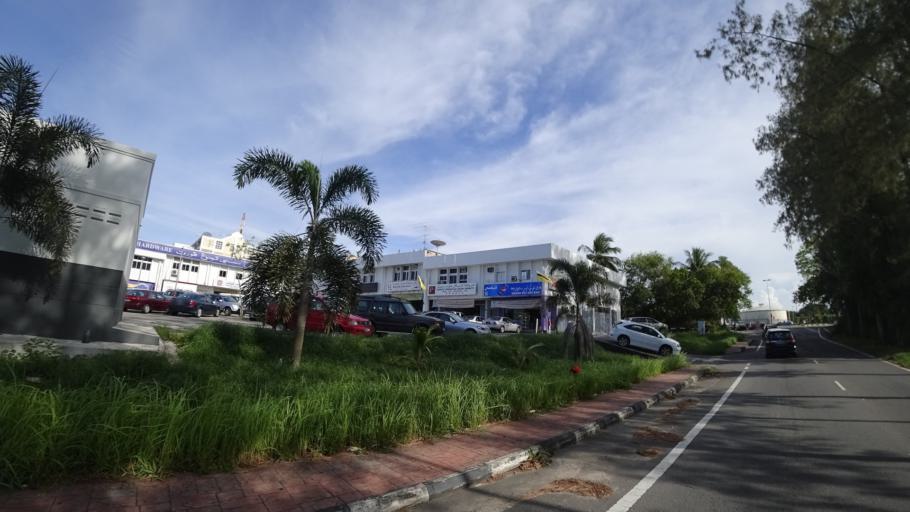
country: BN
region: Brunei and Muara
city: Bandar Seri Begawan
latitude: 4.9103
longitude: 114.9127
